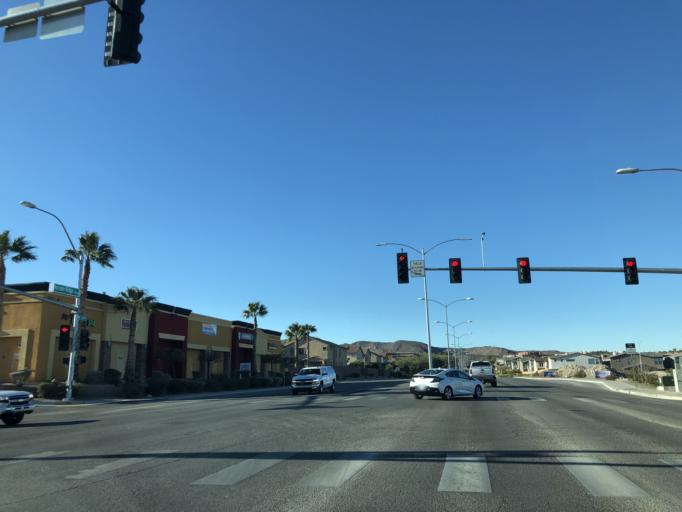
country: US
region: Nevada
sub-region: Clark County
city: Whitney
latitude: 36.0158
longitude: -115.0564
